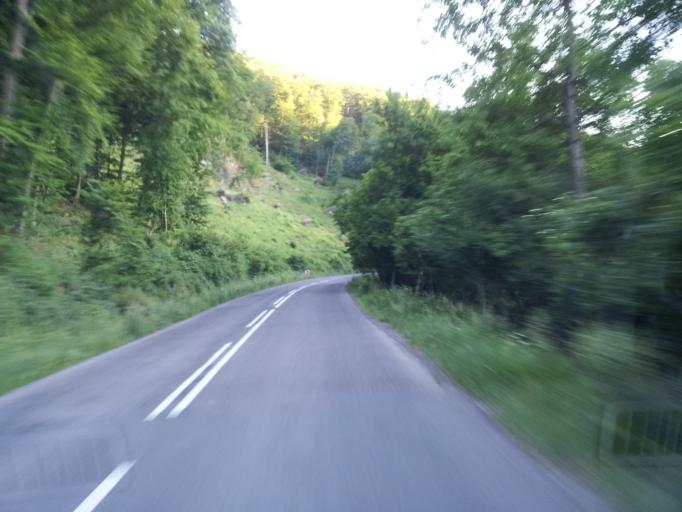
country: SK
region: Banskobystricky
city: Krupina
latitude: 48.3141
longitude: 18.9777
